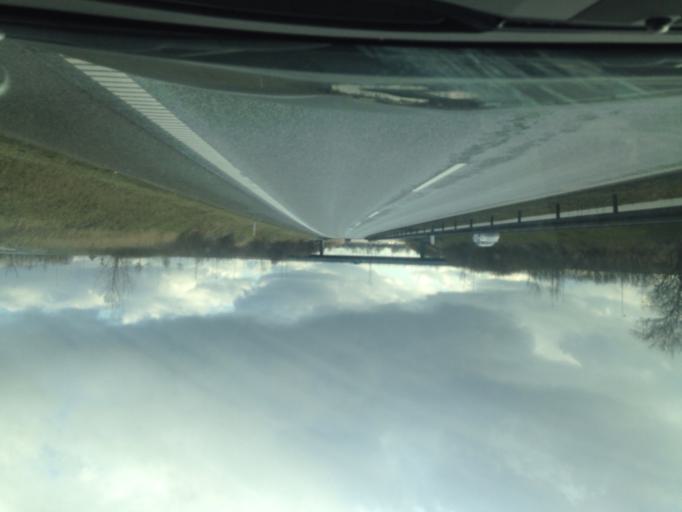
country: DK
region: South Denmark
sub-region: Kerteminde Kommune
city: Langeskov
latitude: 55.3581
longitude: 10.5540
